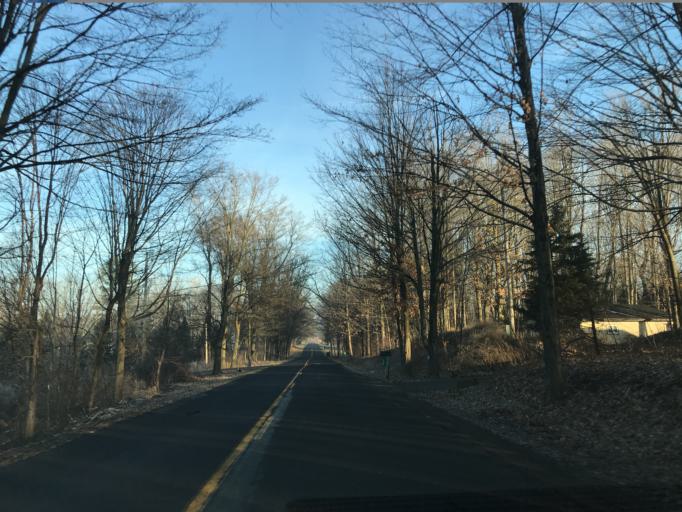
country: US
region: Michigan
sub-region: Ingham County
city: Holt
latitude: 42.5768
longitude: -84.5822
